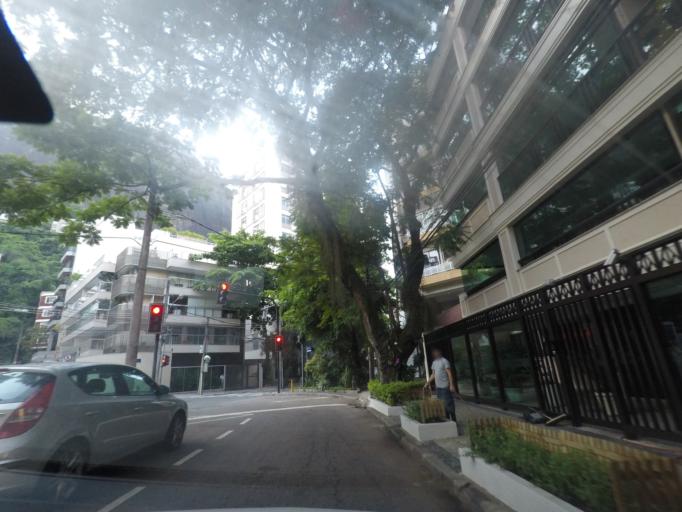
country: BR
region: Rio de Janeiro
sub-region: Rio De Janeiro
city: Rio de Janeiro
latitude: -22.9661
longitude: -43.2025
